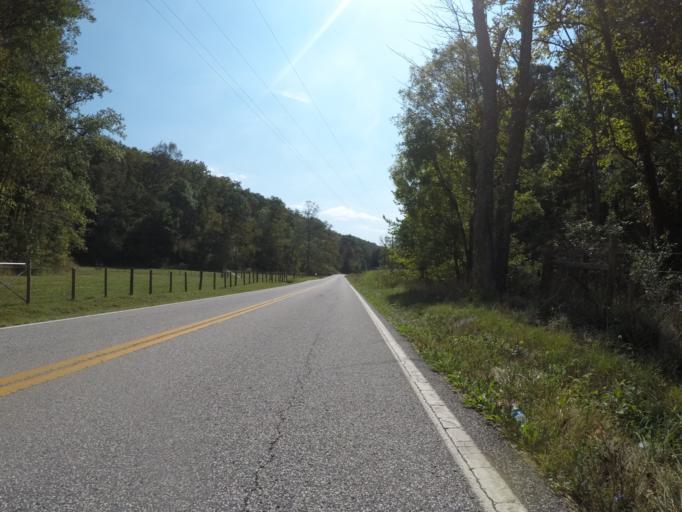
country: US
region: West Virginia
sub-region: Cabell County
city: Lesage
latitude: 38.5770
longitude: -82.4086
